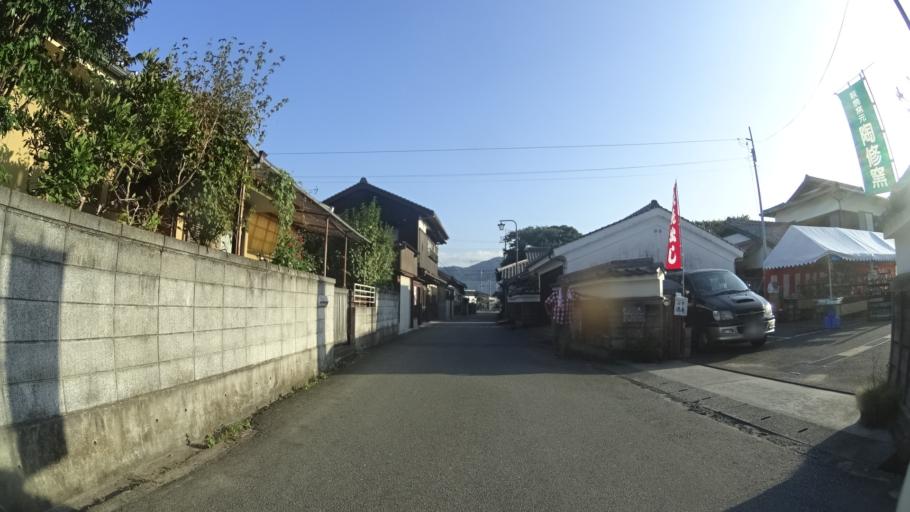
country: JP
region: Yamaguchi
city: Hagi
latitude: 34.4112
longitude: 131.3947
